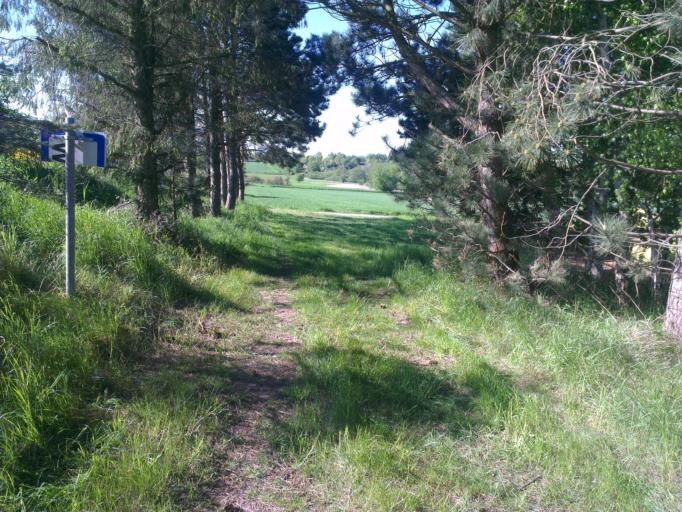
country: DK
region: Capital Region
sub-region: Frederikssund Kommune
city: Jaegerspris
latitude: 55.8397
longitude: 11.9765
